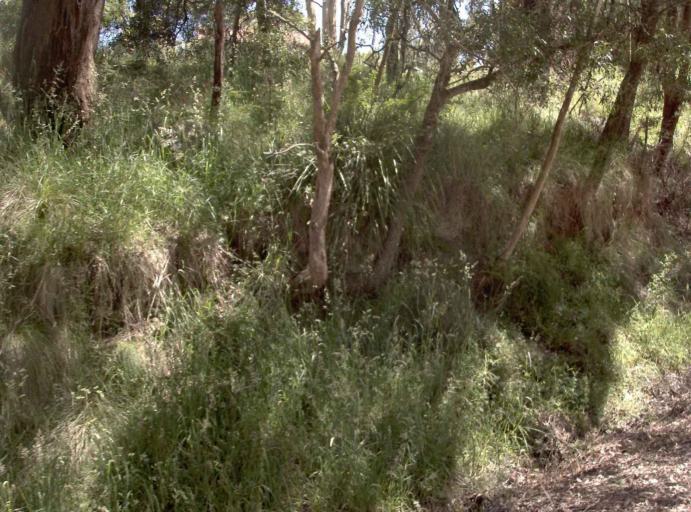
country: AU
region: Victoria
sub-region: East Gippsland
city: Lakes Entrance
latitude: -37.2228
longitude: 148.2637
